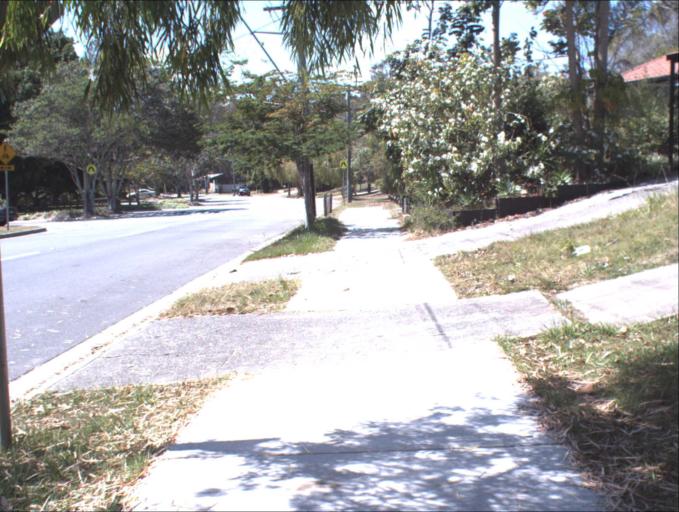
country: AU
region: Queensland
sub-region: Logan
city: Springwood
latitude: -27.6010
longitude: 153.1445
